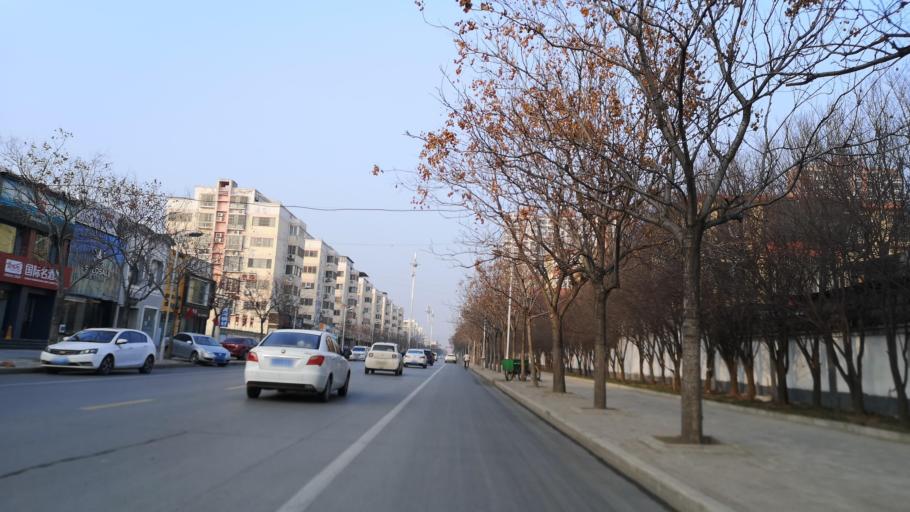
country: CN
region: Henan Sheng
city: Zhongyuanlu
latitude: 35.7705
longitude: 115.0641
